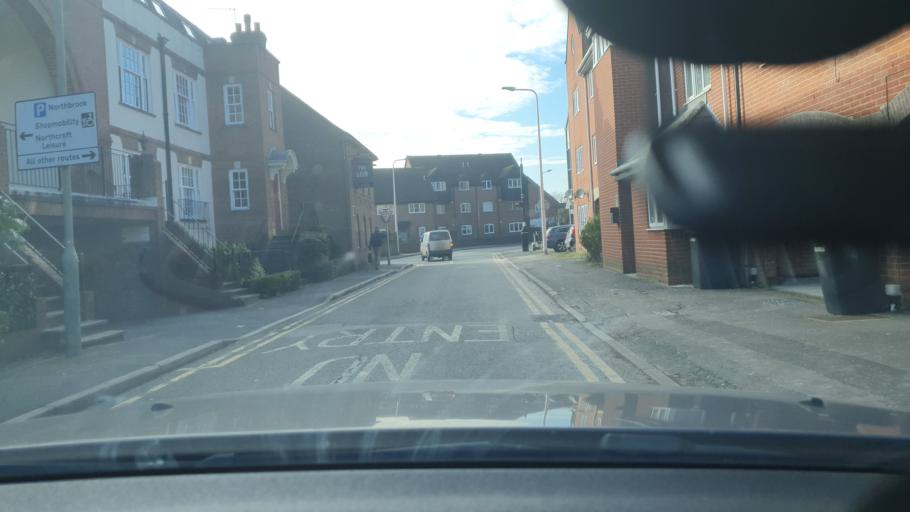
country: GB
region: England
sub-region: West Berkshire
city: Newbury
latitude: 51.4040
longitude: -1.3262
